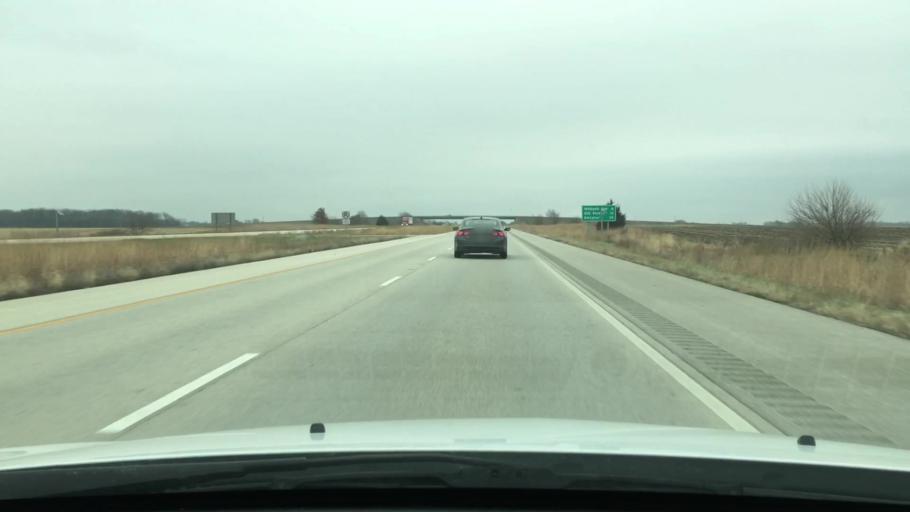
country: US
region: Illinois
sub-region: Sangamon County
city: New Berlin
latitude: 39.7402
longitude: -89.9079
